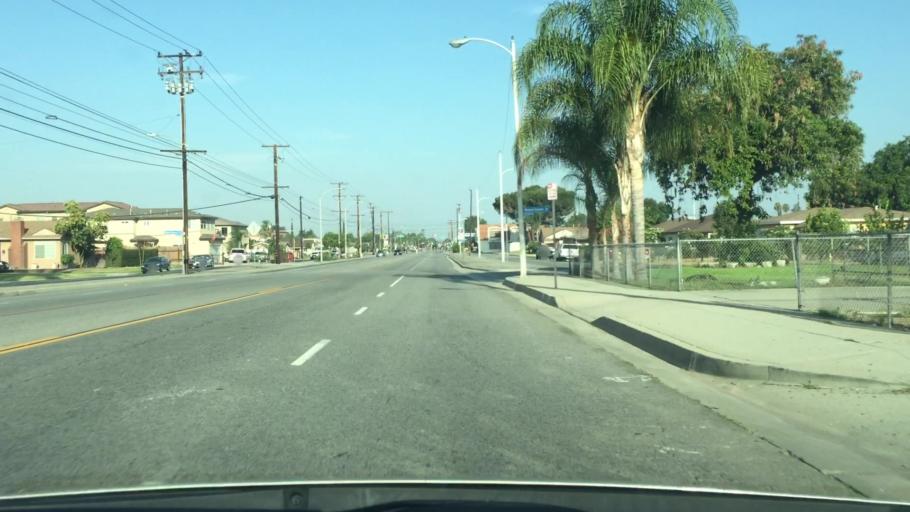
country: US
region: California
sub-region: Los Angeles County
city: Irwindale
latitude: 34.0898
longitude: -117.9304
